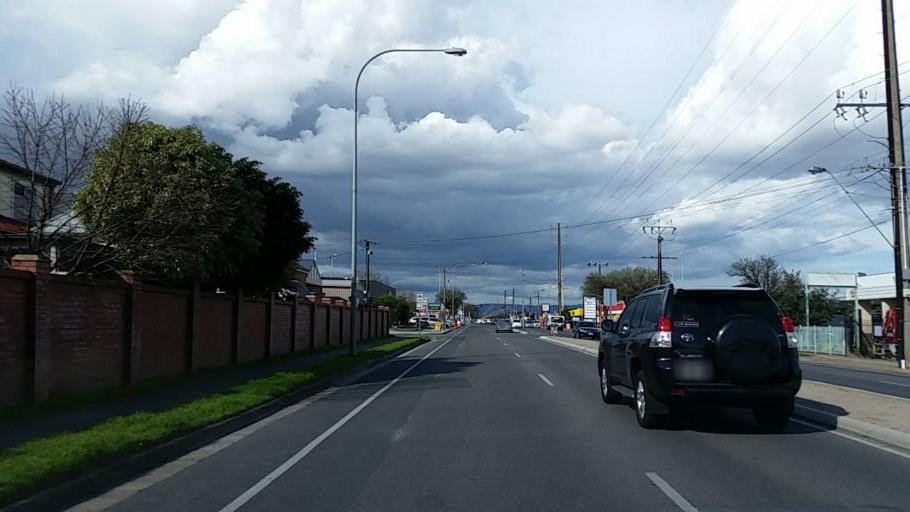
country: AU
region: South Australia
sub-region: Charles Sturt
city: Findon
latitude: -34.9056
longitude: 138.5294
